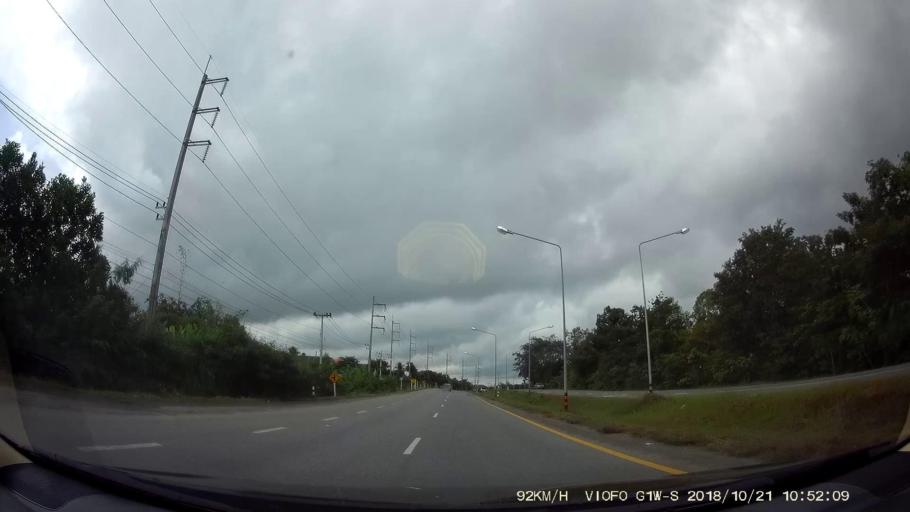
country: TH
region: Chaiyaphum
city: Khon Sawan
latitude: 15.9789
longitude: 102.1965
